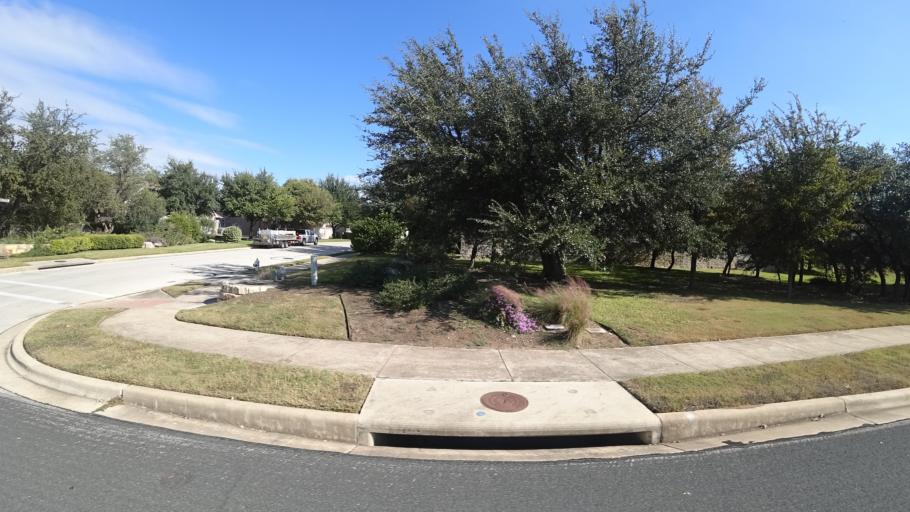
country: US
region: Texas
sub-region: Travis County
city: Hudson Bend
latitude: 30.3780
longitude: -97.9043
